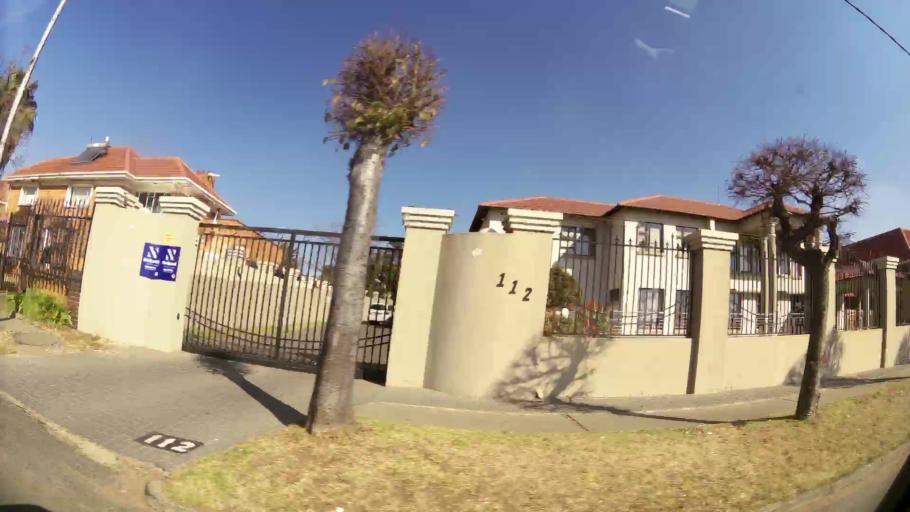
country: ZA
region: Gauteng
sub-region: City of Johannesburg Metropolitan Municipality
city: Johannesburg
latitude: -26.2571
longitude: 28.0641
